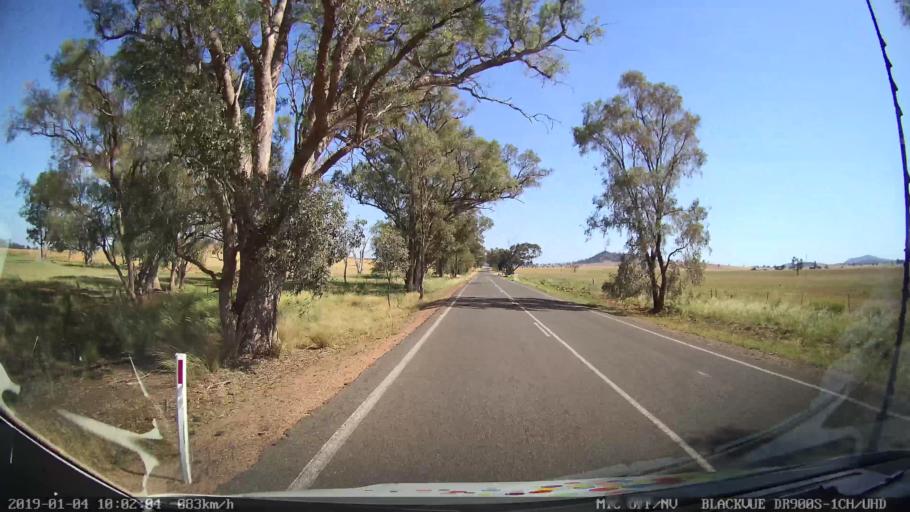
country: AU
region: New South Wales
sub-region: Cabonne
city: Canowindra
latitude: -33.4809
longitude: 148.3662
